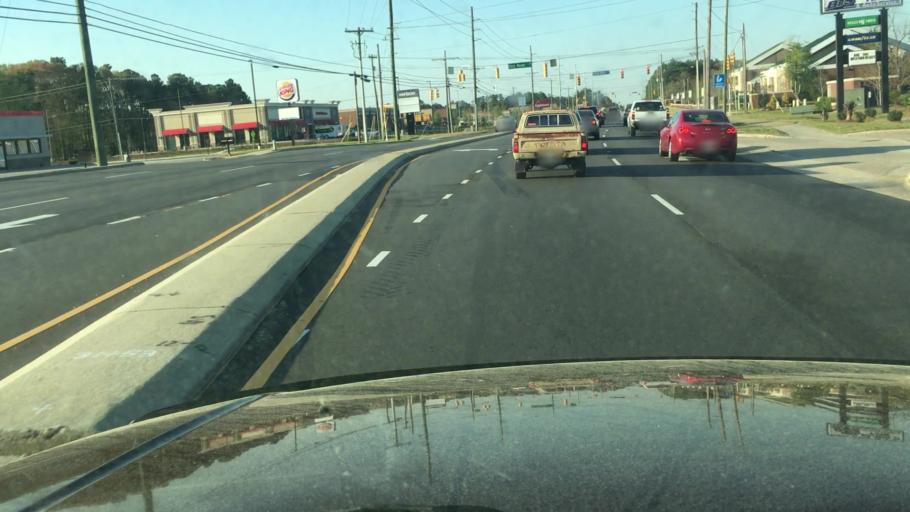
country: US
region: North Carolina
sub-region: Cumberland County
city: Fayetteville
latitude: 35.1289
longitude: -78.8789
